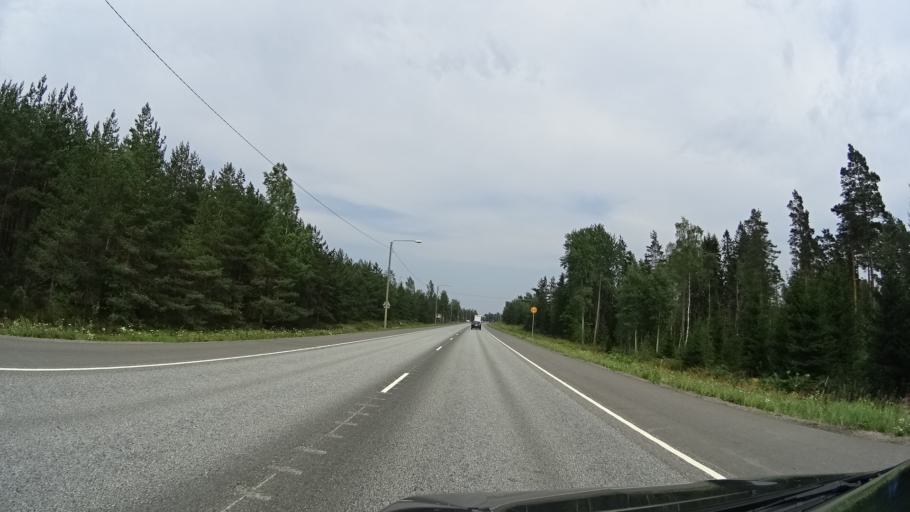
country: FI
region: Uusimaa
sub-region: Raaseporin
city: Ekenaes
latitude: 60.0021
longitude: 23.5208
